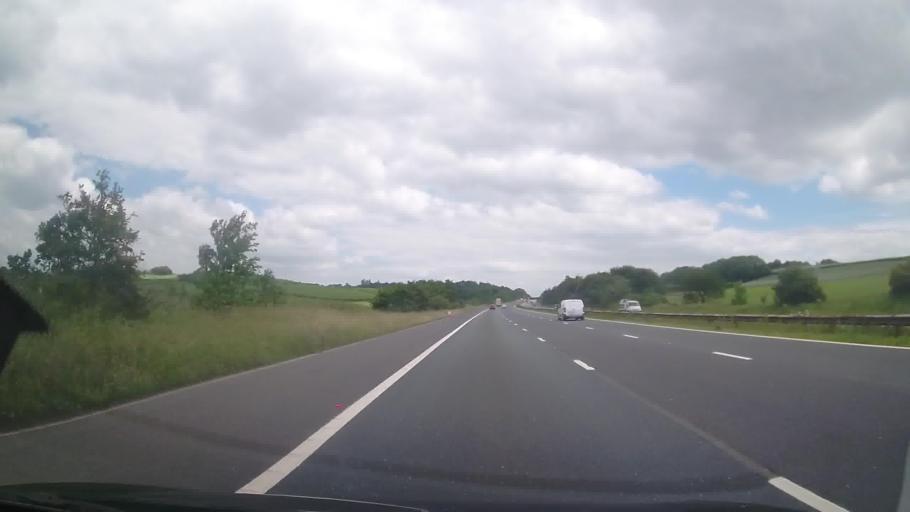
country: GB
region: England
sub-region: Devon
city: Uffculme
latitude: 50.9345
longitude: -3.3219
